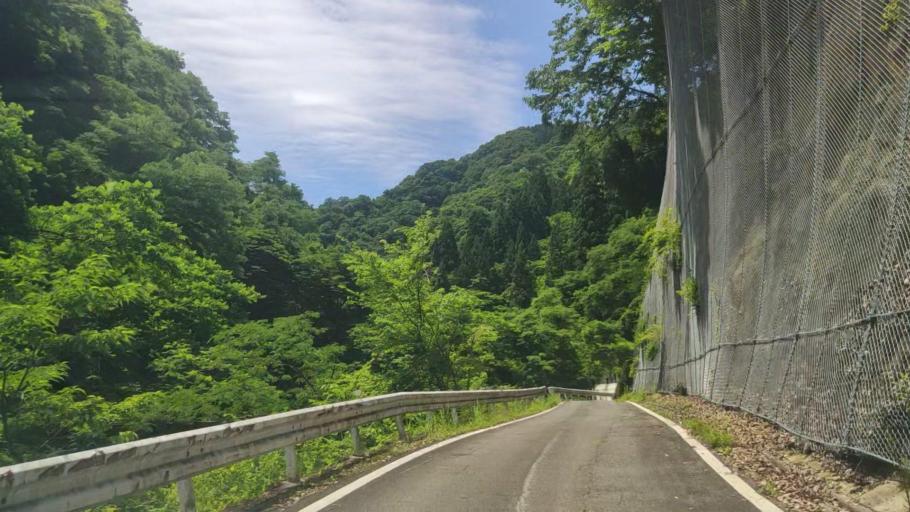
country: JP
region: Tottori
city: Tottori
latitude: 35.4097
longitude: 134.5073
